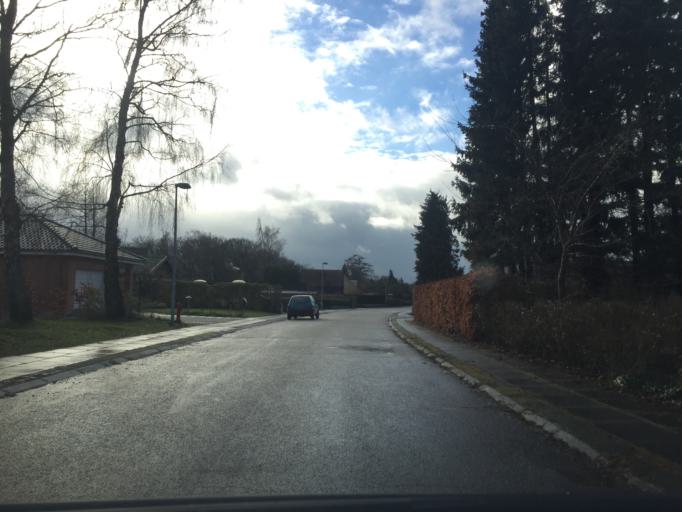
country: DK
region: Capital Region
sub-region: Fureso Kommune
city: Stavnsholt
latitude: 55.8095
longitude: 12.3992
